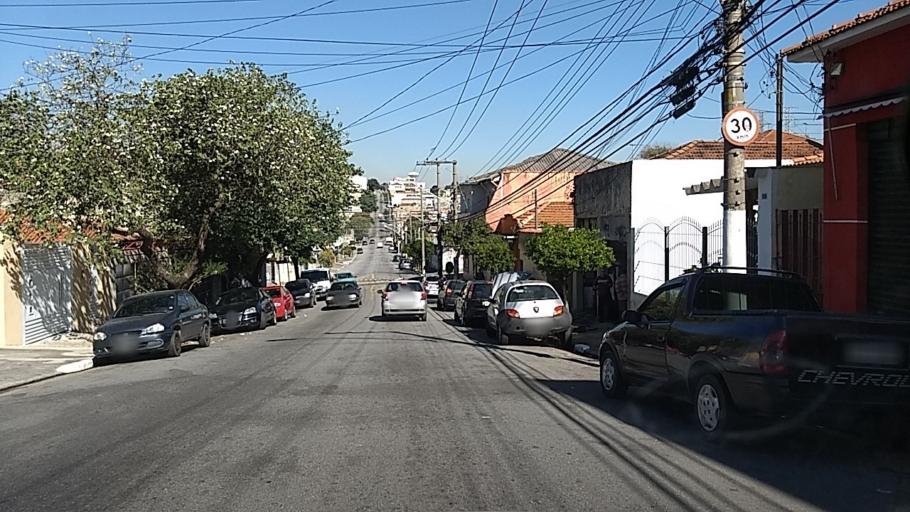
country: BR
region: Sao Paulo
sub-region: Guarulhos
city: Guarulhos
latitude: -23.4915
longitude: -46.5810
